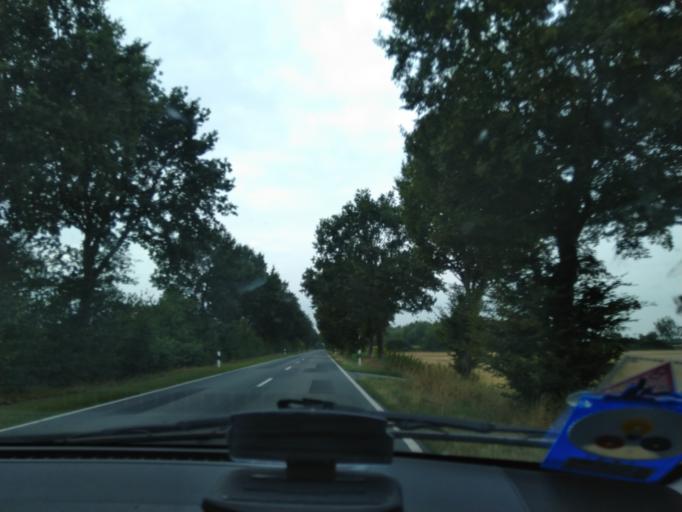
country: DE
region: Lower Saxony
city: Rhede
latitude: 53.0700
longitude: 7.2064
